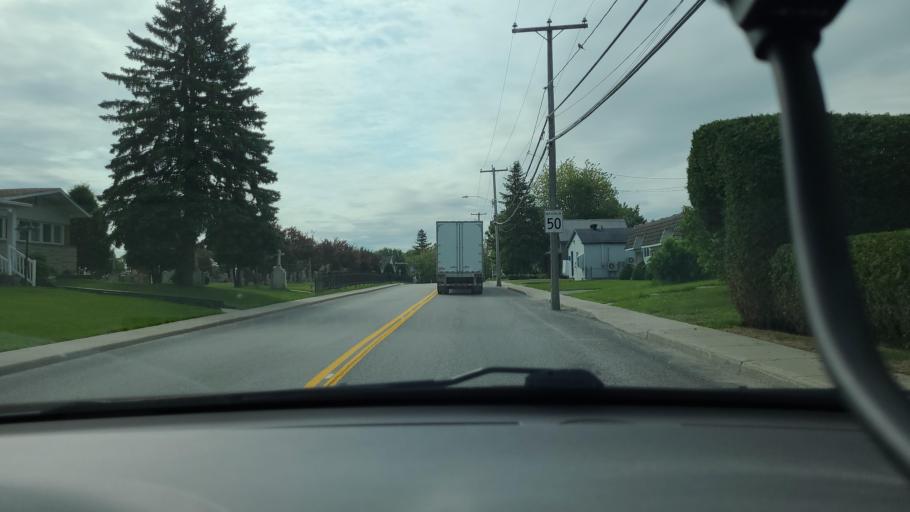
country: CA
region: Quebec
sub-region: Lanaudiere
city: Crabtree
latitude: 45.9664
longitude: -73.4769
